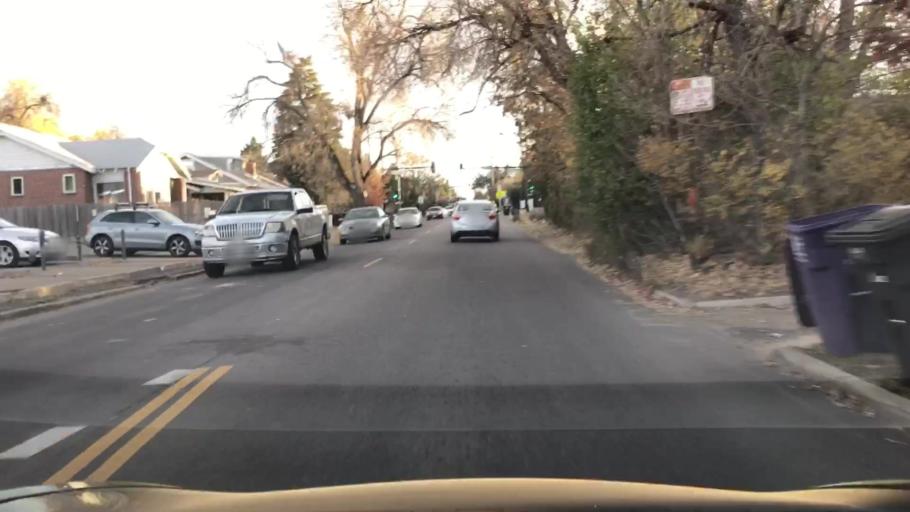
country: US
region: Colorado
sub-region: Arapahoe County
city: Glendale
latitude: 39.7397
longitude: -104.9035
